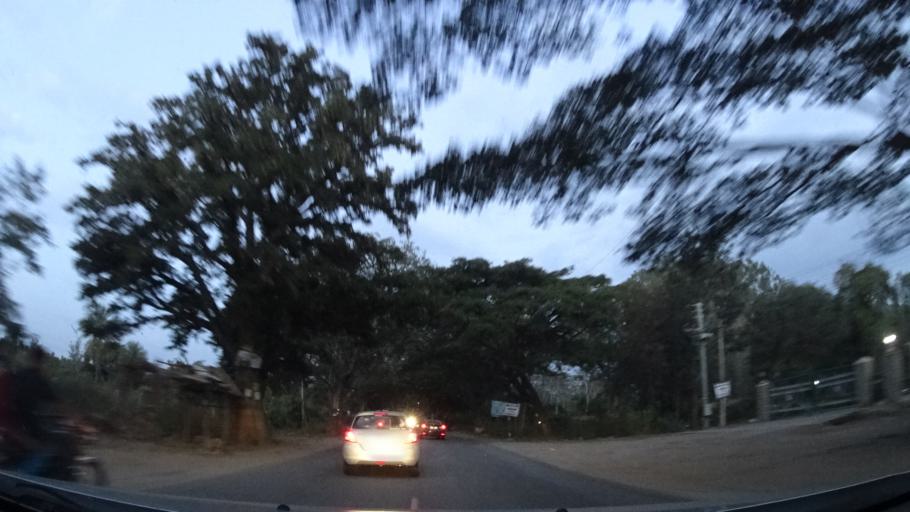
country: IN
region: Karnataka
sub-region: Bangalore Urban
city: Anekal
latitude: 12.7827
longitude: 77.4998
